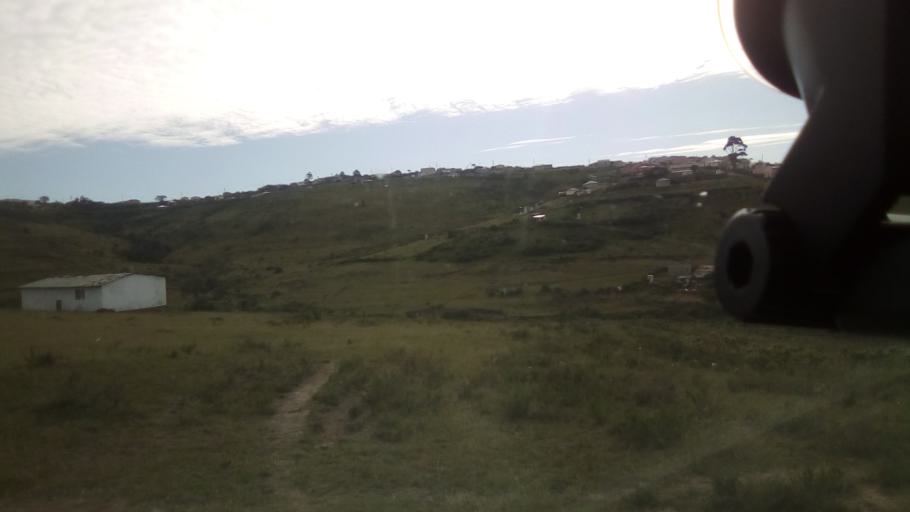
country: ZA
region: Eastern Cape
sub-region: Buffalo City Metropolitan Municipality
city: East London
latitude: -32.7995
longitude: 27.9650
